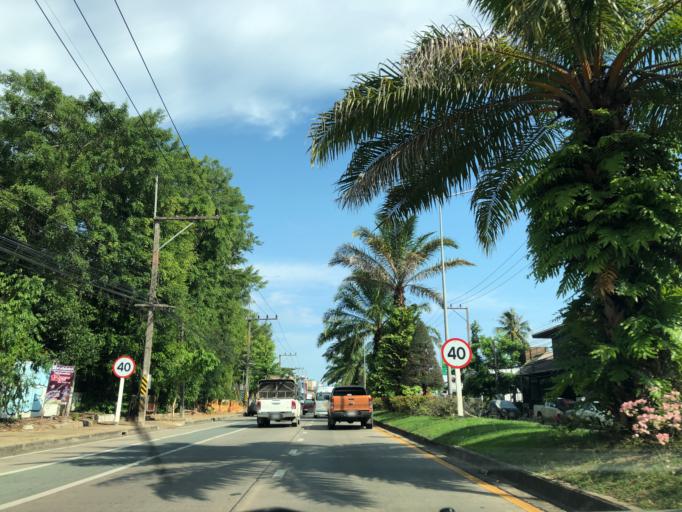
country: TH
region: Krabi
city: Krabi
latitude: 8.0838
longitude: 98.9141
